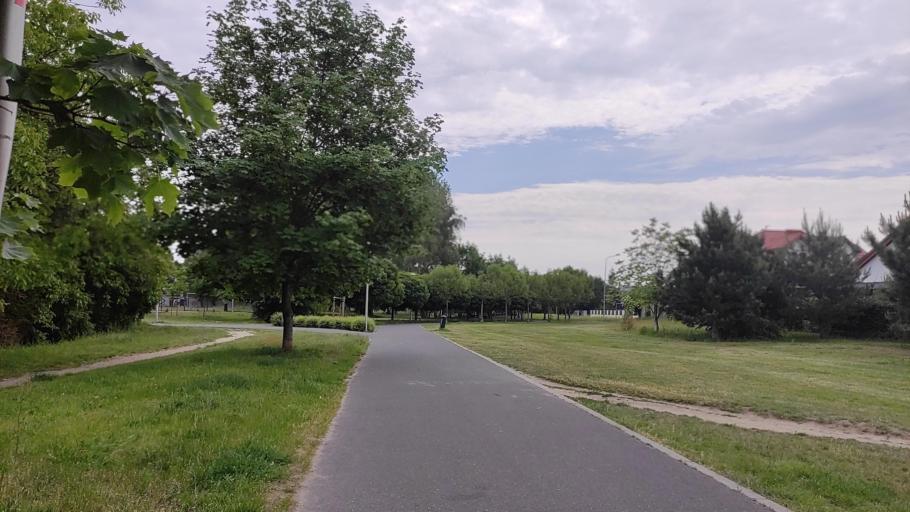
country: PL
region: Greater Poland Voivodeship
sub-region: Powiat poznanski
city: Swarzedz
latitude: 52.3991
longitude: 17.0723
